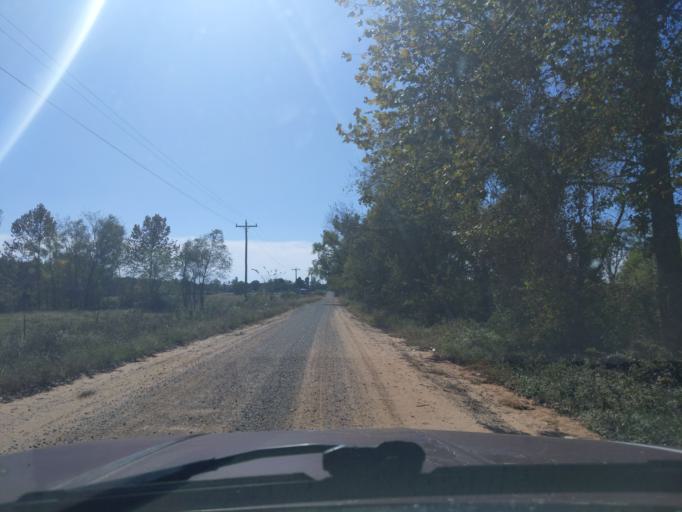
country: US
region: Oklahoma
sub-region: Creek County
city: Bristow
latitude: 35.6673
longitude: -96.4234
